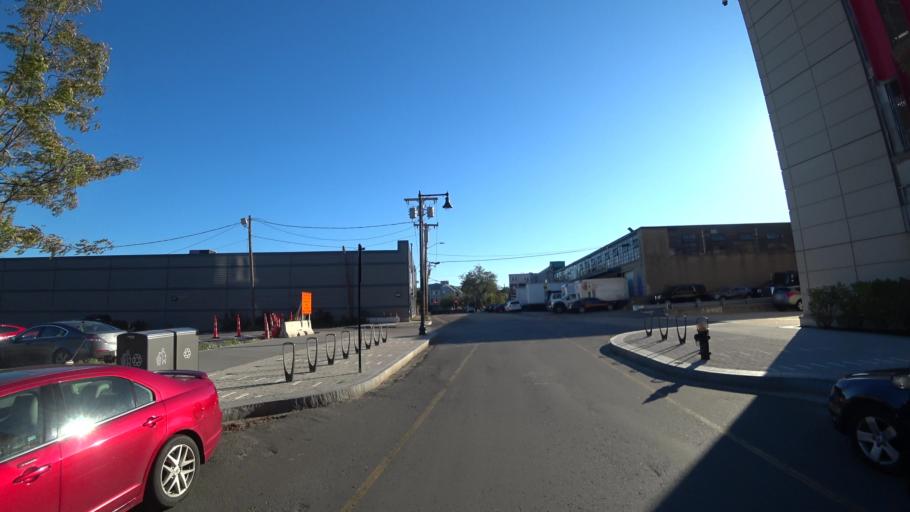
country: US
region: Massachusetts
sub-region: Norfolk County
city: Brookline
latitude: 42.3565
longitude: -71.1458
